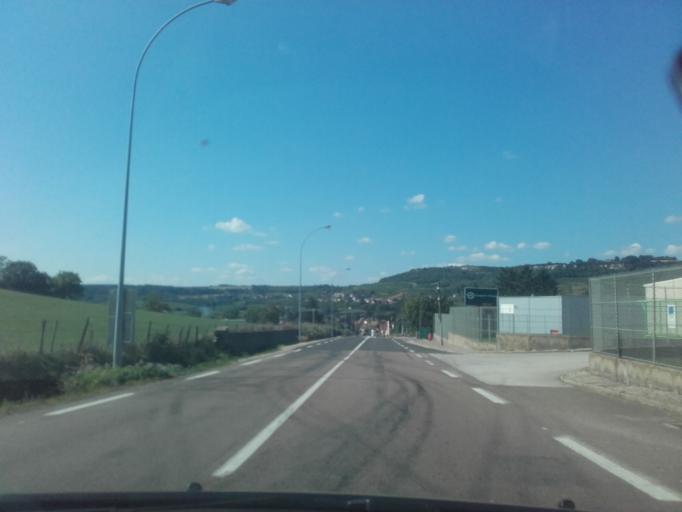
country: FR
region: Bourgogne
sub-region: Departement de la Cote-d'Or
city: Nolay
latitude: 46.9471
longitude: 4.6432
